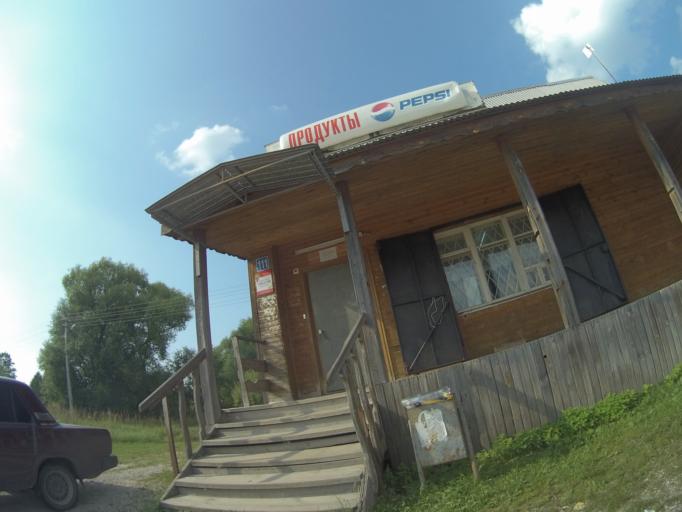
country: RU
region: Vladimir
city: Andreyevo
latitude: 55.9434
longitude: 41.0833
